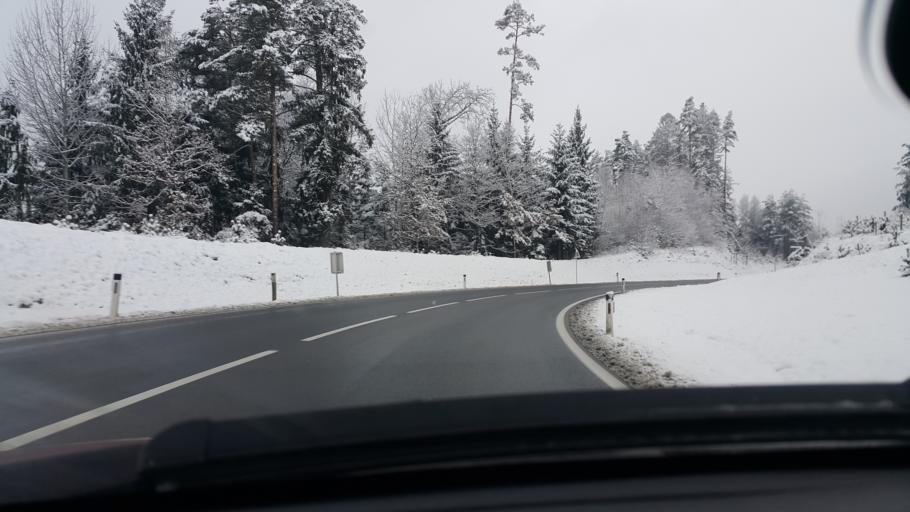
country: AT
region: Styria
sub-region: Politischer Bezirk Voitsberg
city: Mooskirchen
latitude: 47.0046
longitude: 15.2674
